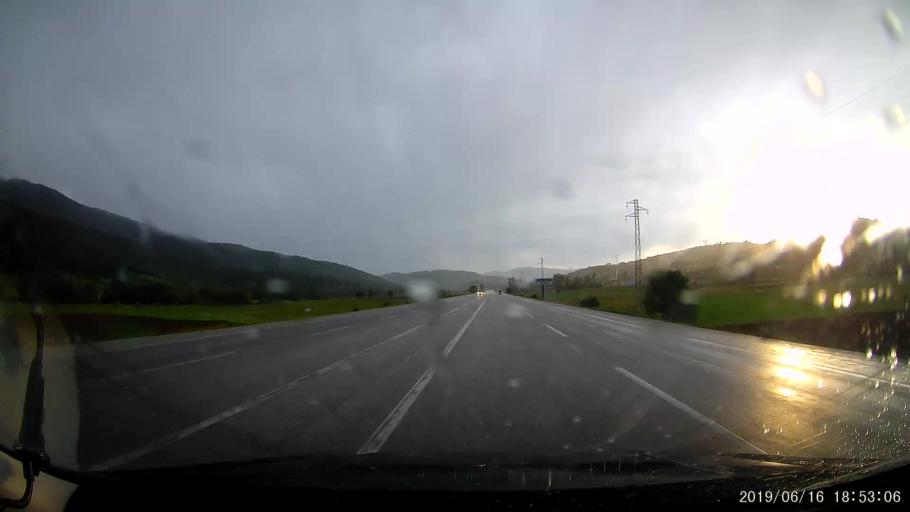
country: TR
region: Erzincan
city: Catalcam
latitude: 39.8998
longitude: 38.8855
